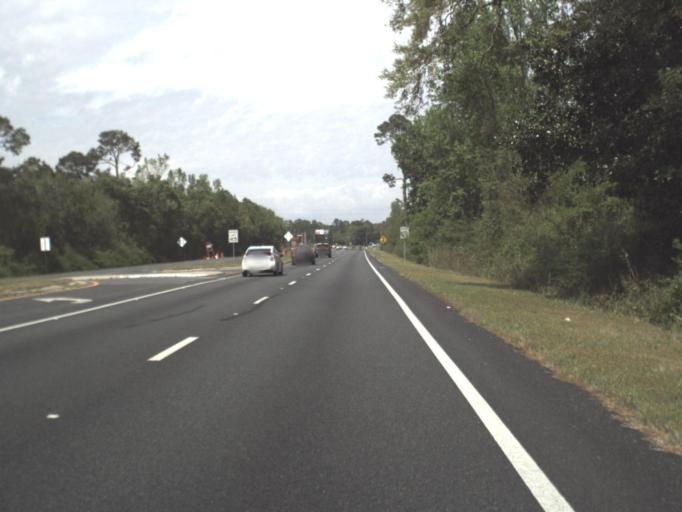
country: US
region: Florida
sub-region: Santa Rosa County
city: Pace
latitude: 30.5865
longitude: -87.1774
